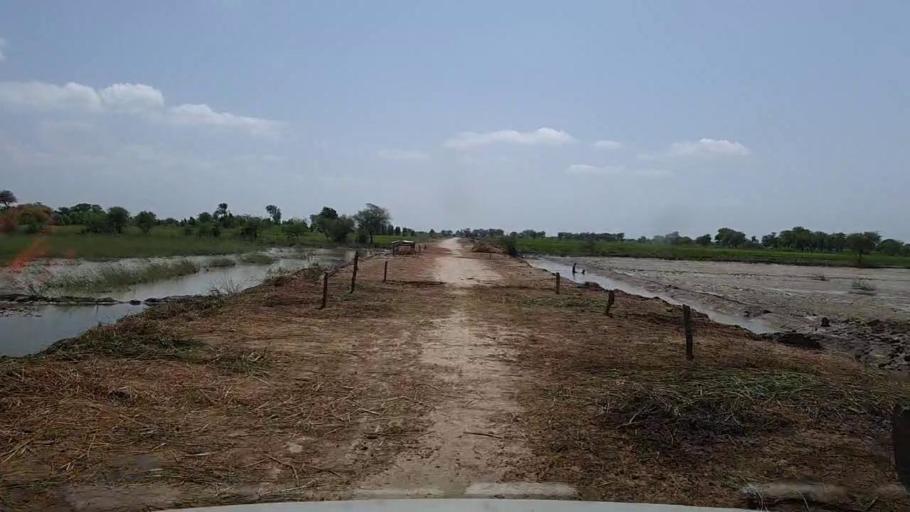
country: PK
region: Sindh
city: Kario
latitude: 24.6881
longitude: 68.5940
